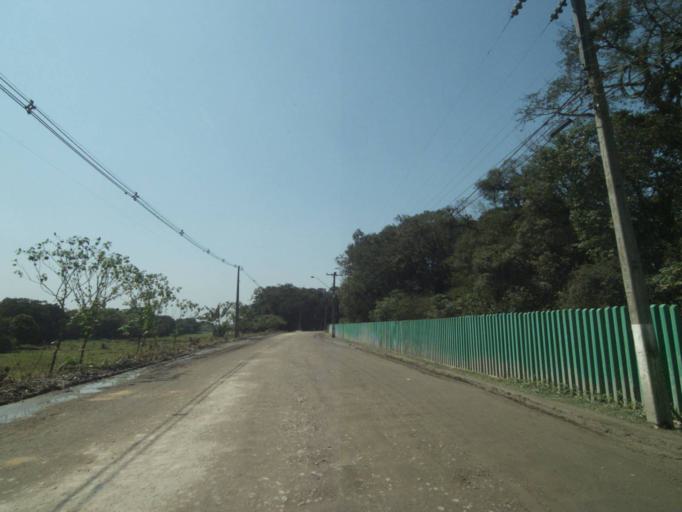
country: BR
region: Parana
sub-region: Paranagua
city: Paranagua
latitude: -25.5474
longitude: -48.5751
